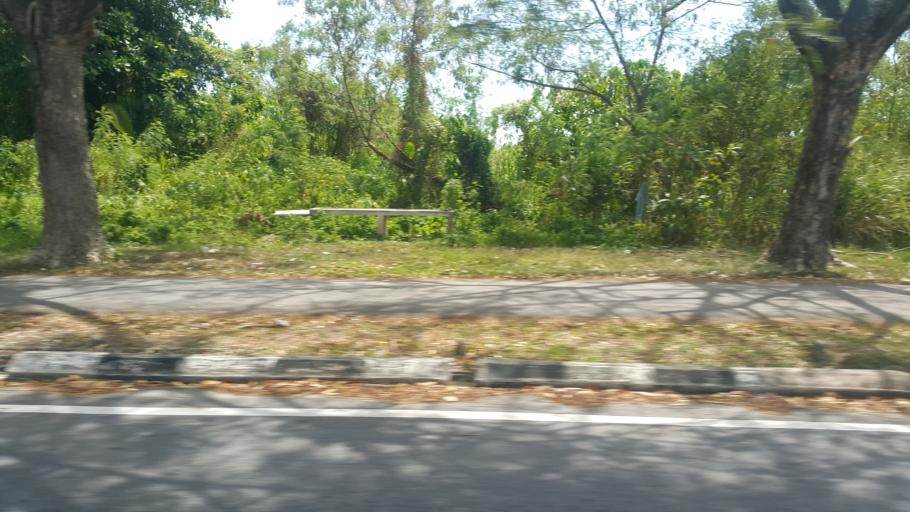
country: MY
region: Melaka
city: Kampung Bukit Baharu
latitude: 2.1883
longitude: 102.2783
